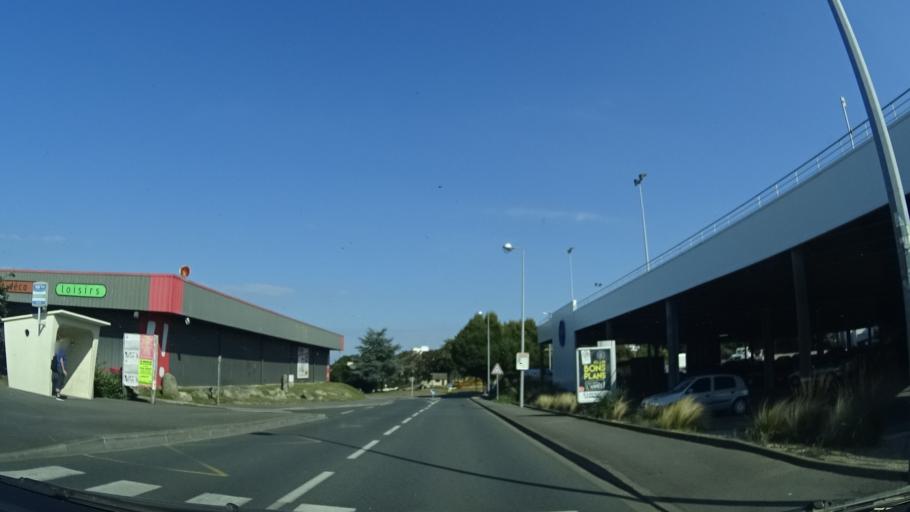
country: FR
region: Brittany
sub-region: Departement du Finistere
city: Douarnenez
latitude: 48.0916
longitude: -4.3460
